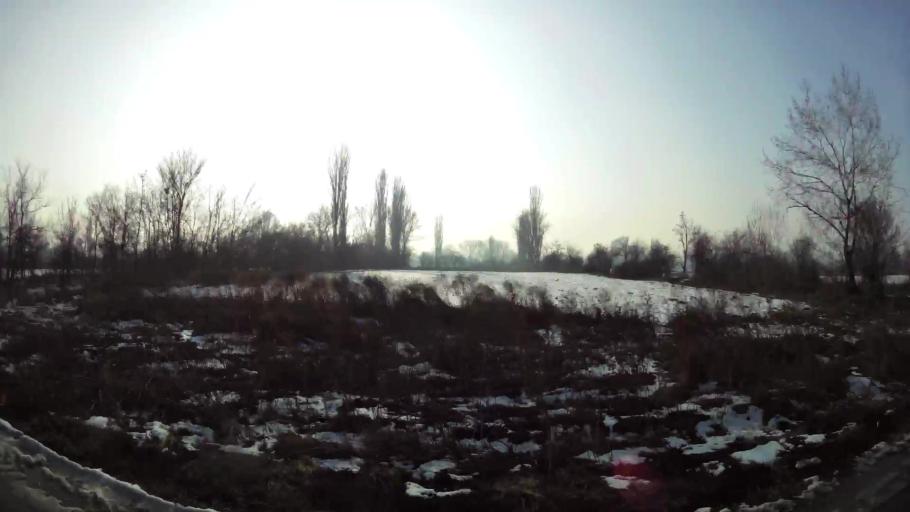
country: MK
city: Kadino
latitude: 41.9655
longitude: 21.5934
